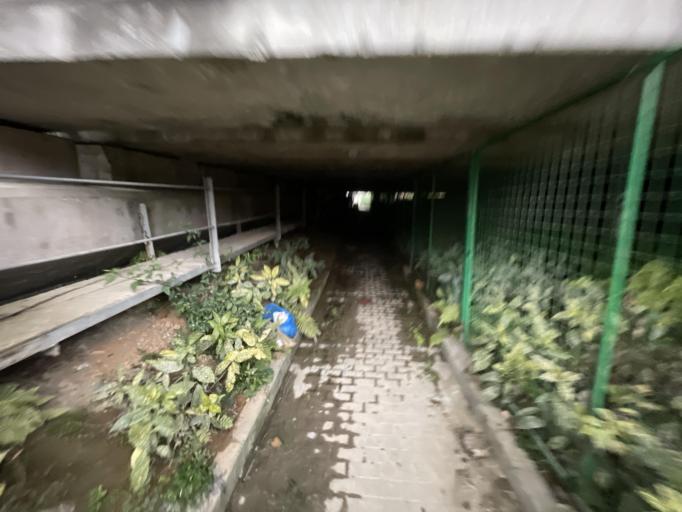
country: CN
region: Zhejiang Sheng
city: Louqiao
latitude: 27.9812
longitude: 120.6195
